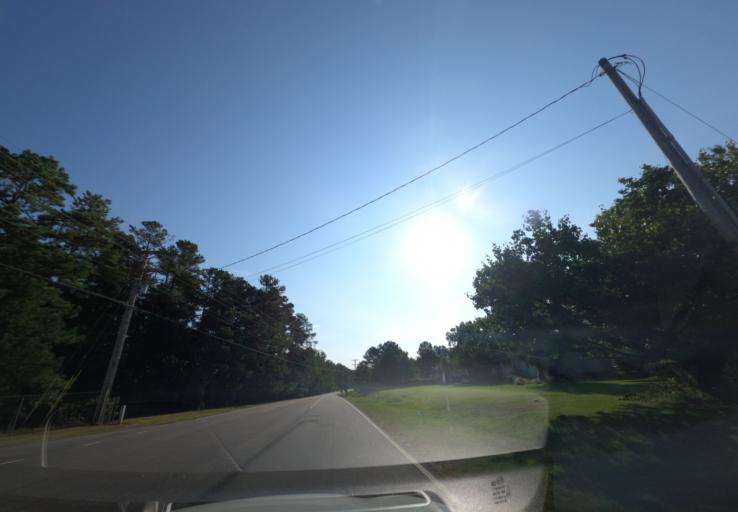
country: US
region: South Carolina
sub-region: Edgefield County
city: Murphys Estates
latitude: 33.5843
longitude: -81.9808
